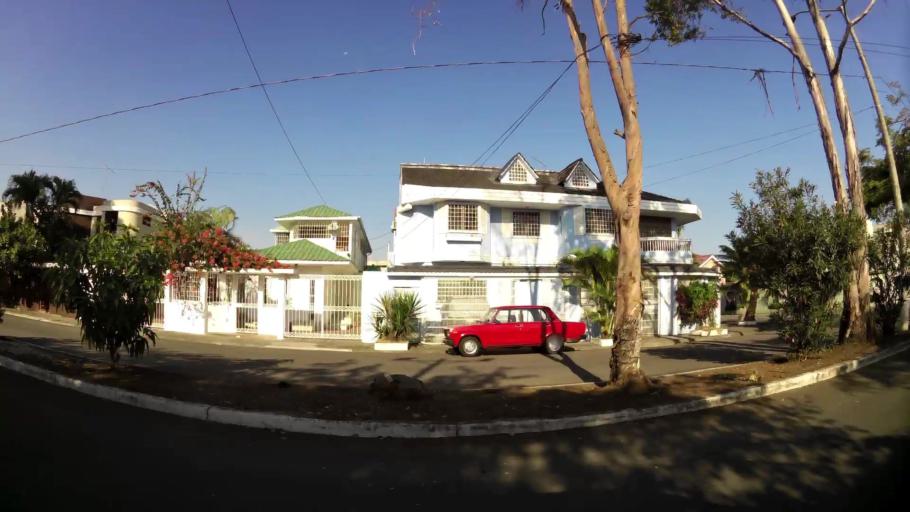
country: EC
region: Guayas
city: Santa Lucia
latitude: -2.1884
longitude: -79.9714
